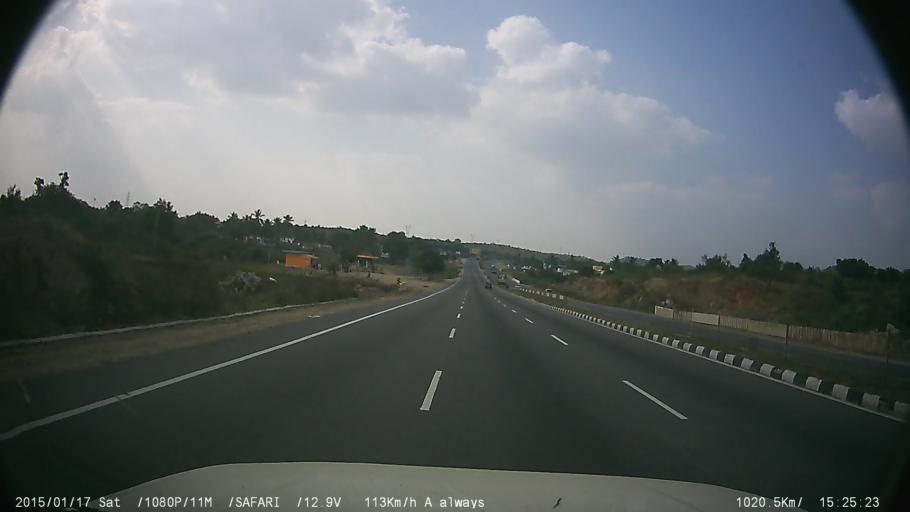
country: IN
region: Tamil Nadu
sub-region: Krishnagiri
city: Krishnagiri
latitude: 12.6146
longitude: 78.0879
